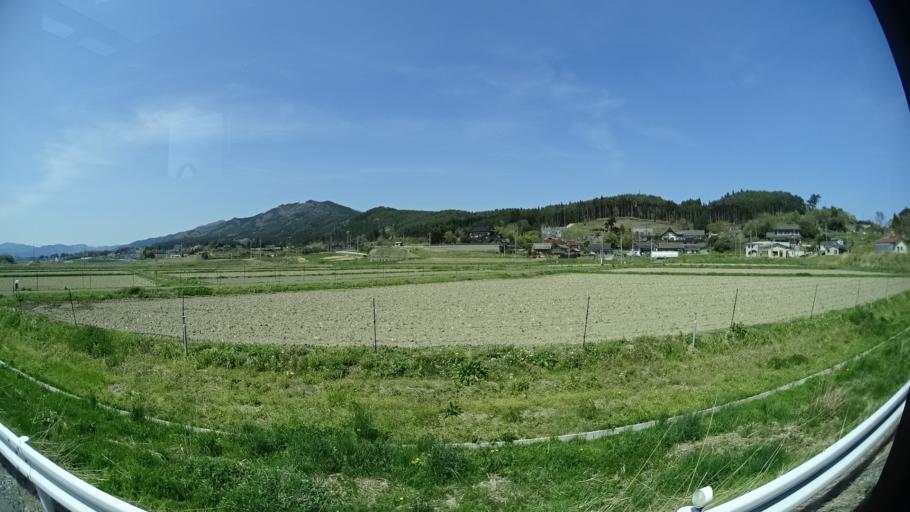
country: JP
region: Iwate
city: Ofunato
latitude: 38.9877
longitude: 141.7048
